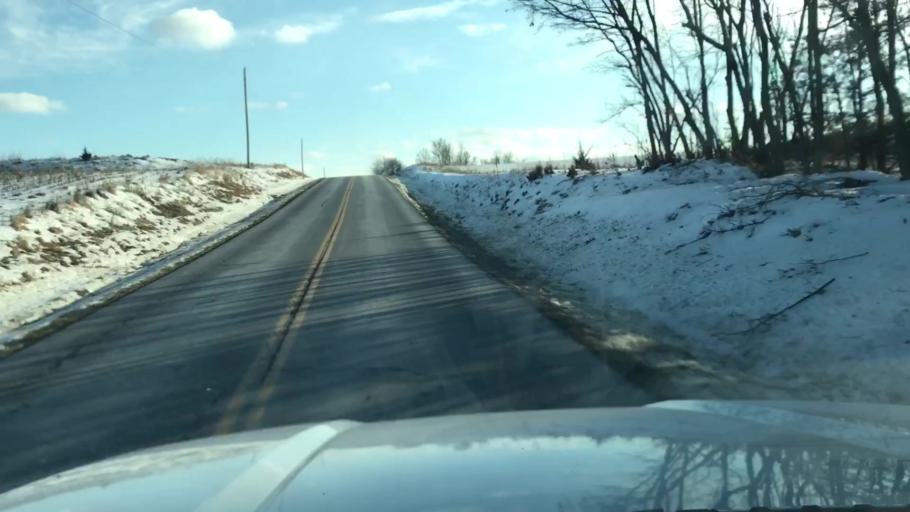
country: US
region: Missouri
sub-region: Holt County
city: Oregon
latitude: 40.0536
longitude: -94.9749
